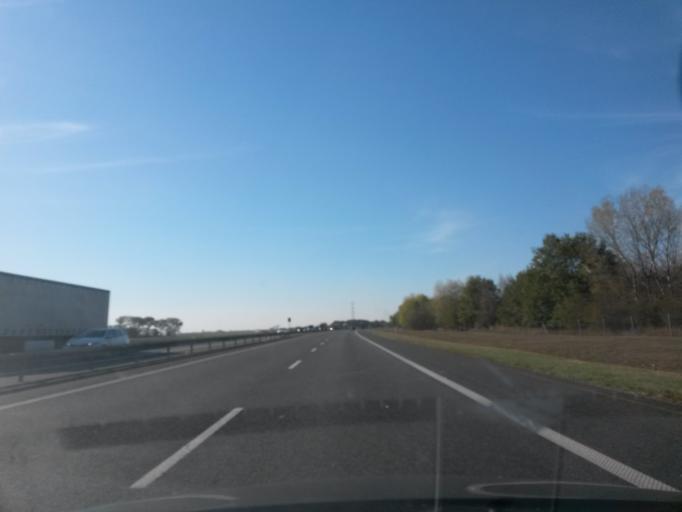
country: PL
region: Opole Voivodeship
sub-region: Powiat brzeski
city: Grodkow
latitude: 50.7699
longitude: 17.3878
